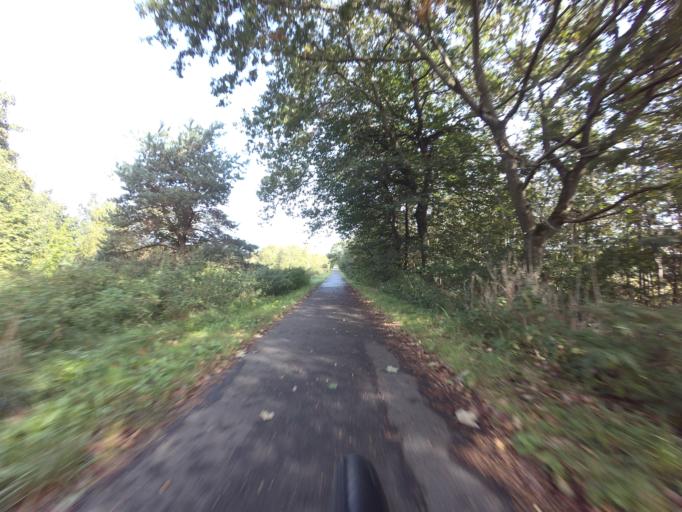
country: DK
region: Central Jutland
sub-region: Viborg Kommune
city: Viborg
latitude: 56.4244
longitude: 9.4530
